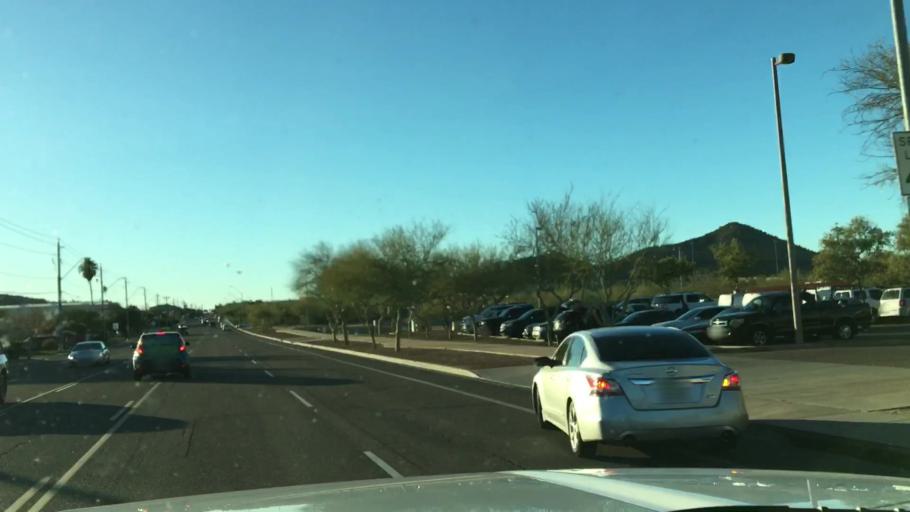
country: US
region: Arizona
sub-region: Maricopa County
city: Paradise Valley
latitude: 33.6696
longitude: -112.0238
